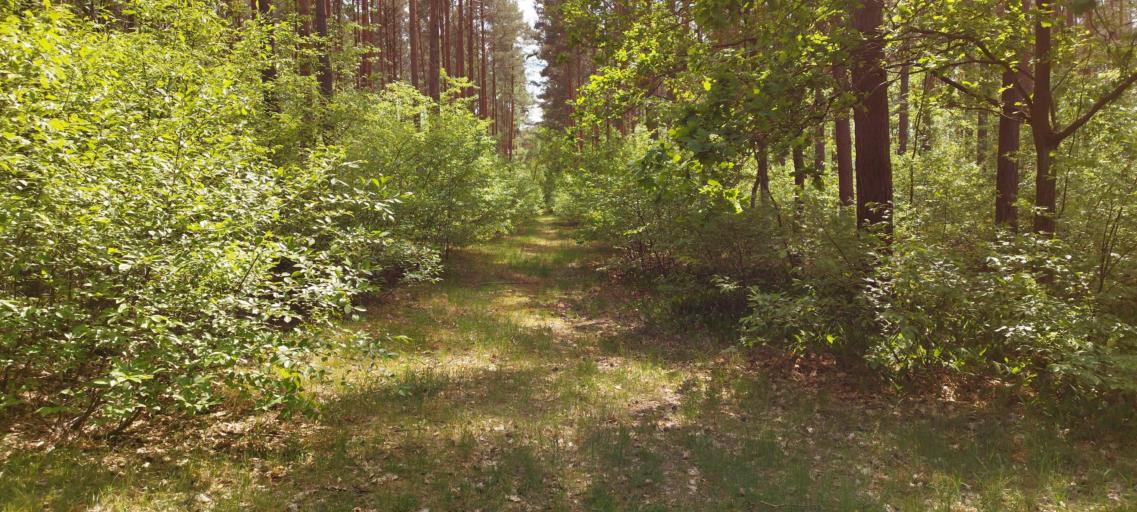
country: DE
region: Brandenburg
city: Rauen
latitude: 52.3662
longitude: 14.0260
